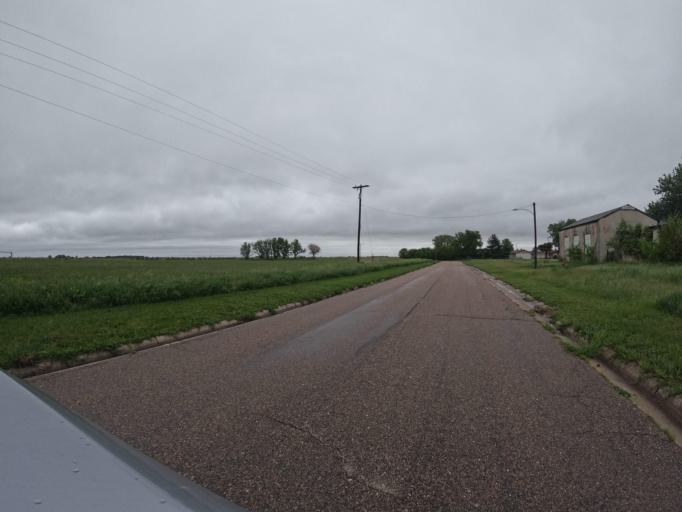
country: US
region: Nebraska
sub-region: Clay County
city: Harvard
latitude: 40.6289
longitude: -98.0914
